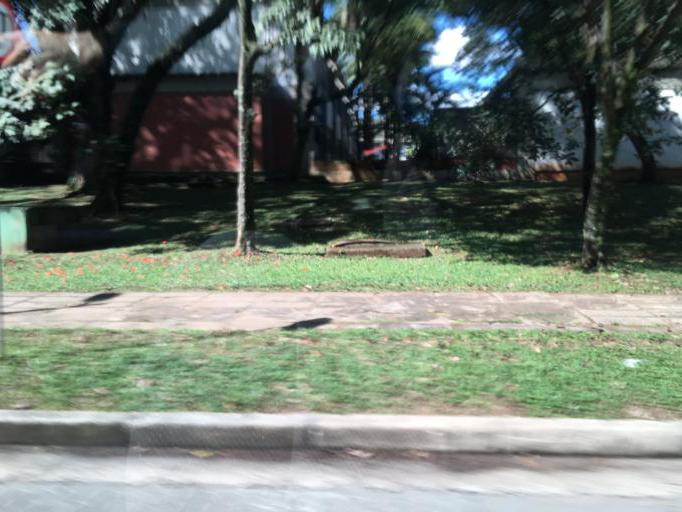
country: BR
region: Sao Paulo
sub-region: Osasco
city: Osasco
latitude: -23.5564
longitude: -46.7340
